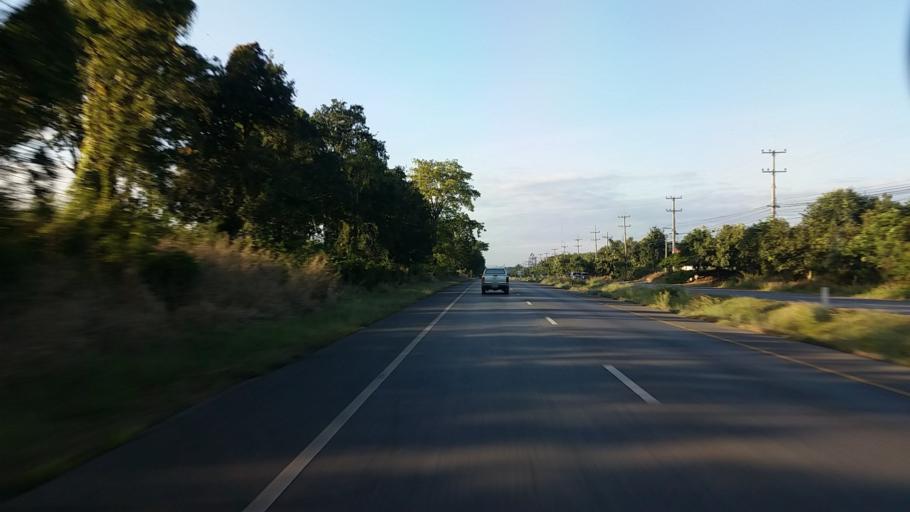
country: TH
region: Lop Buri
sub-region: Amphoe Tha Luang
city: Tha Luang
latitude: 15.1133
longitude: 101.0281
